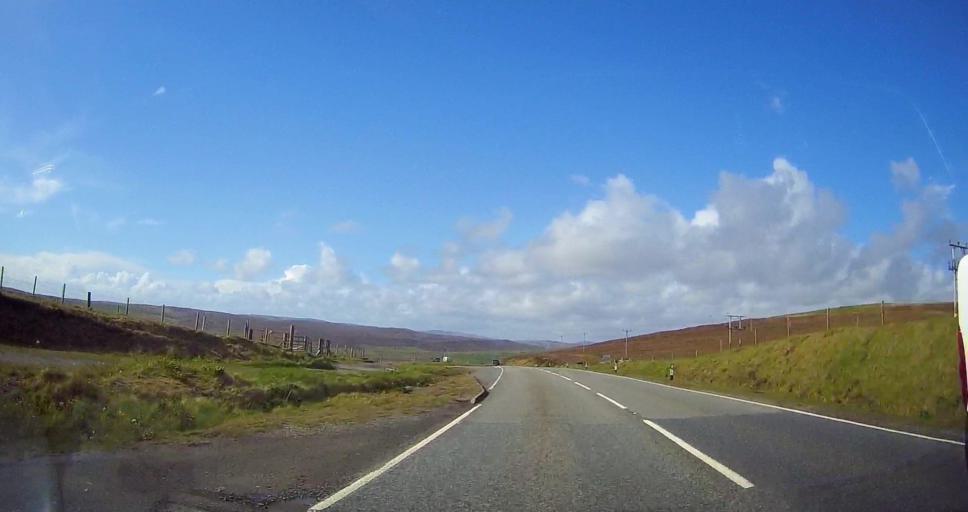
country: GB
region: Scotland
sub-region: Shetland Islands
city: Lerwick
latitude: 60.1756
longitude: -1.2228
